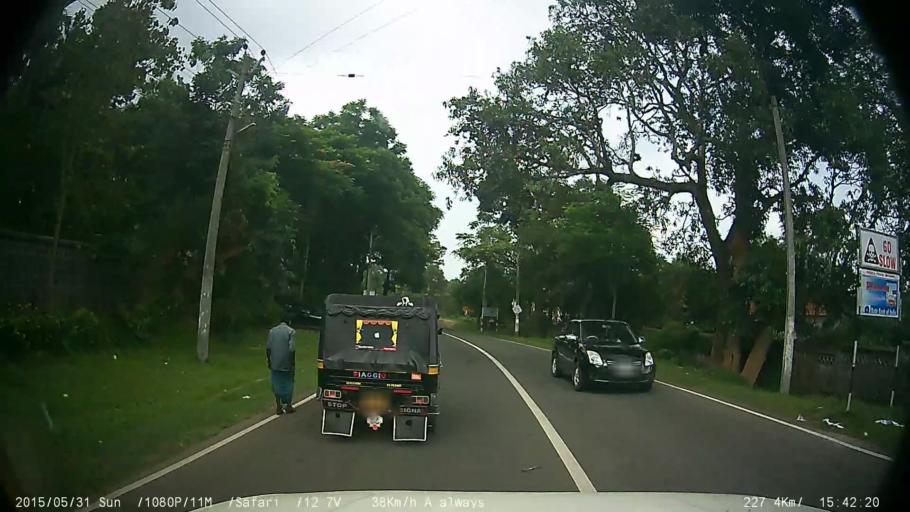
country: IN
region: Kerala
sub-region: Wayanad
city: Panamaram
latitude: 11.6670
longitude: 76.2736
